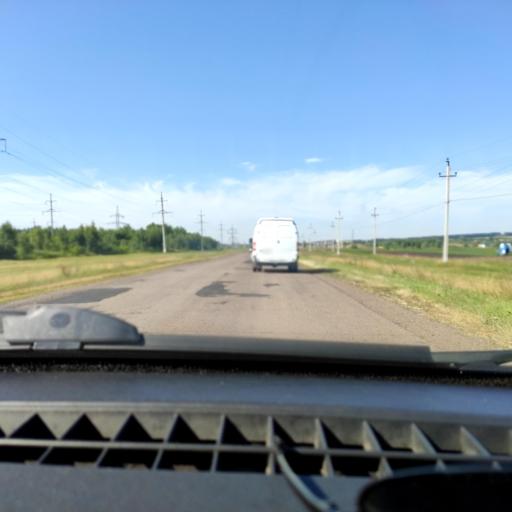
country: RU
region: Bashkortostan
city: Ulukulevo
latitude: 54.4103
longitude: 56.2636
